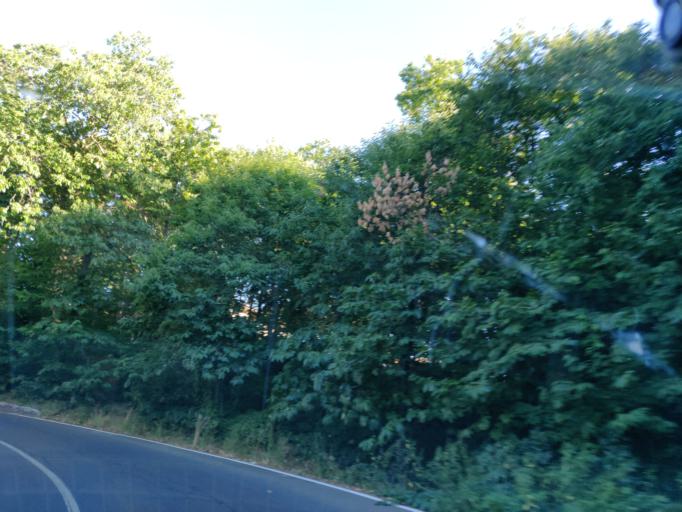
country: IT
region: Tuscany
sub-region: Provincia di Siena
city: Piancastagnaio
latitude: 42.8532
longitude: 11.6845
